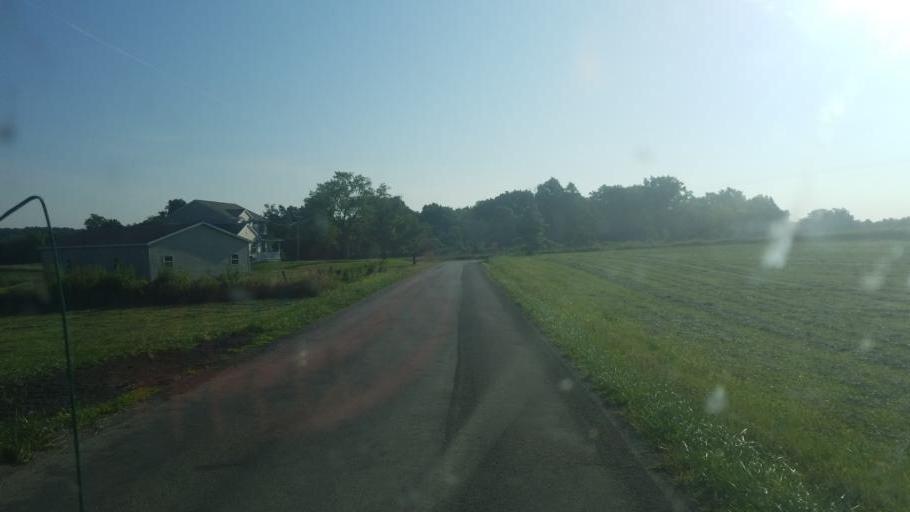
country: US
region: Ohio
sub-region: Ashland County
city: Ashland
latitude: 40.9301
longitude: -82.3408
